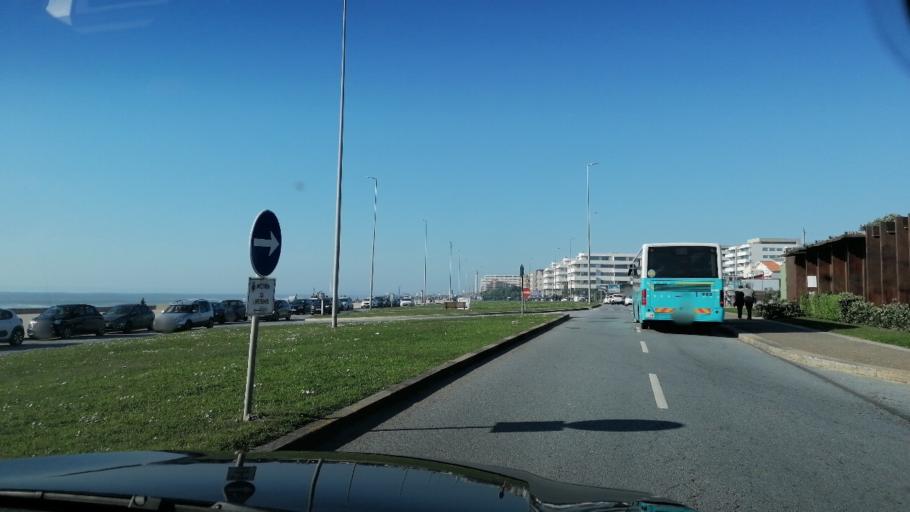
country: PT
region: Porto
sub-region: Matosinhos
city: Leca da Palmeira
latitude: 41.1904
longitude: -8.7050
